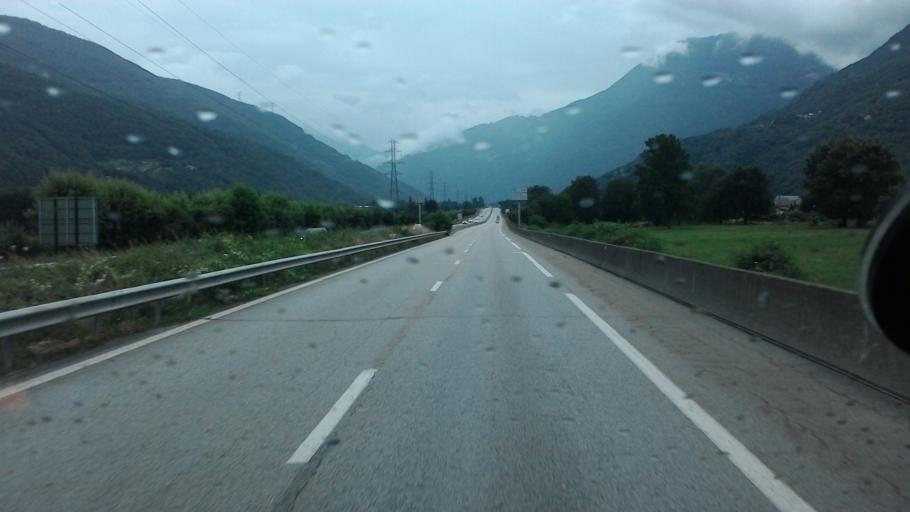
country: FR
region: Rhone-Alpes
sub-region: Departement de la Savoie
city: La Bathie
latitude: 45.6184
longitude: 6.4485
